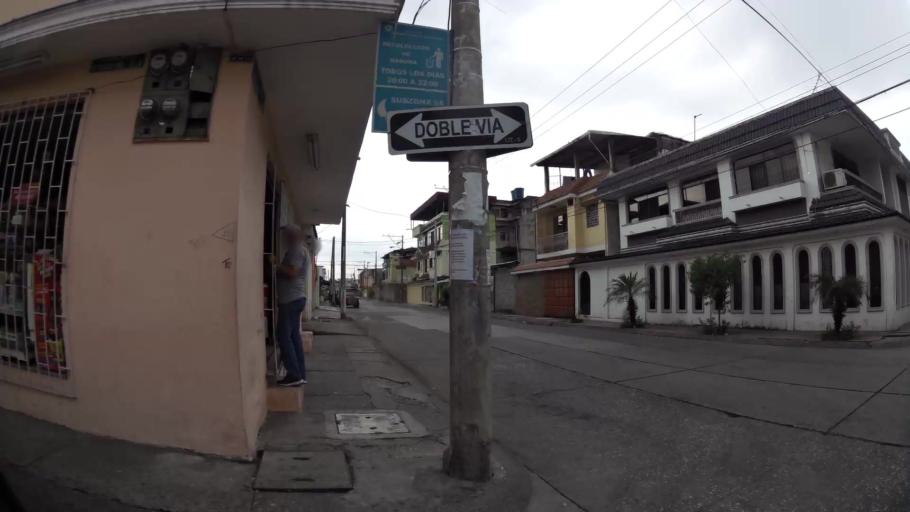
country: EC
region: Guayas
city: Eloy Alfaro
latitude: -2.1210
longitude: -79.8846
